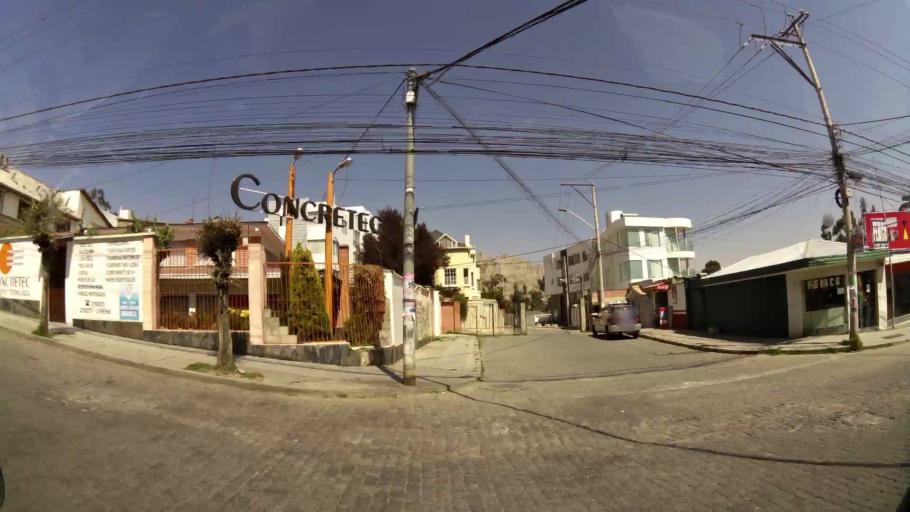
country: BO
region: La Paz
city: La Paz
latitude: -16.5402
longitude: -68.0742
